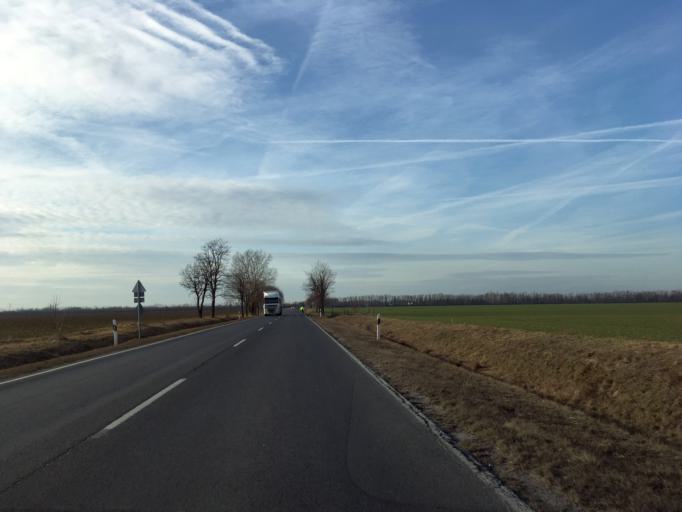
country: HU
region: Gyor-Moson-Sopron
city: Abda
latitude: 47.7107
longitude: 17.5190
